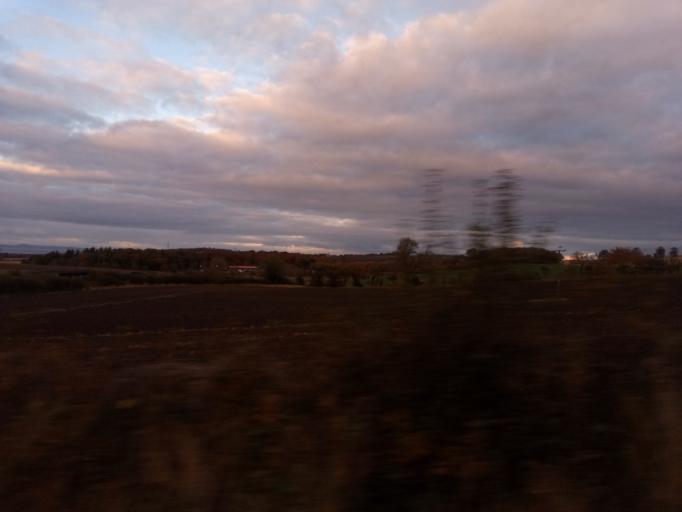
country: GB
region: Scotland
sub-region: Midlothian
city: Dalkeith
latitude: 55.8858
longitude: -3.0291
